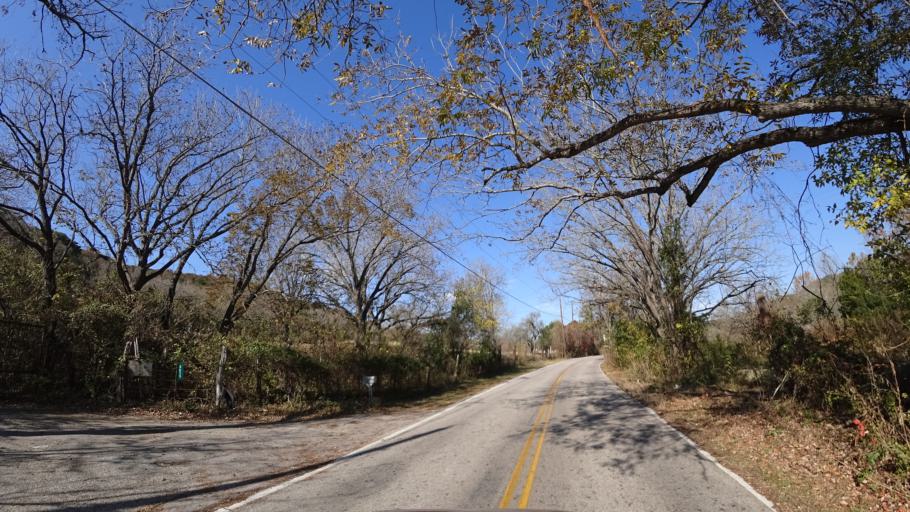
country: US
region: Texas
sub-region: Williamson County
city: Jollyville
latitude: 30.3996
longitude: -97.7832
